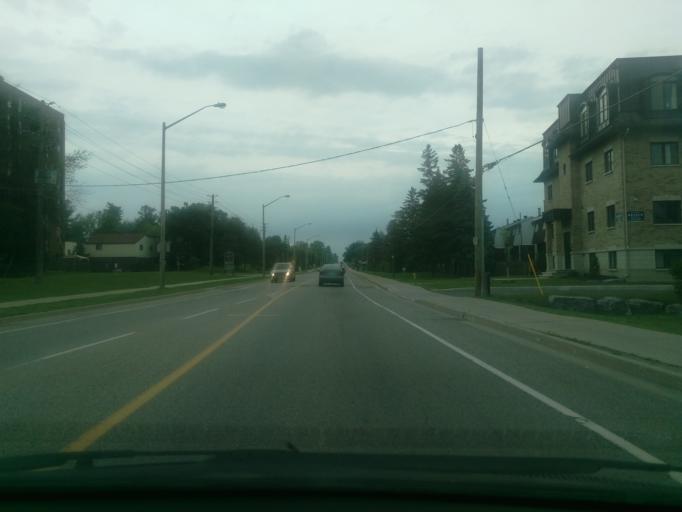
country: CA
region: Ontario
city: Ottawa
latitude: 45.4337
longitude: -75.5595
